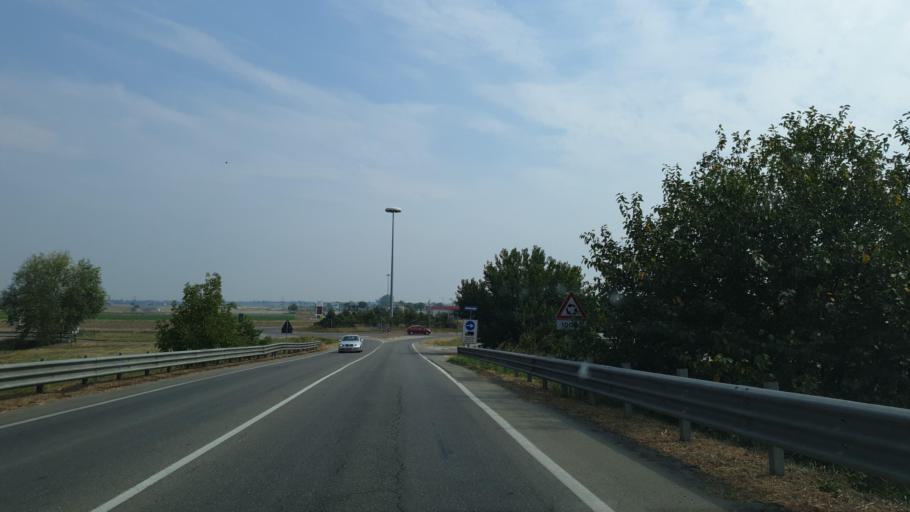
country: IT
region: Emilia-Romagna
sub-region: Provincia di Parma
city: Trecasali
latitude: 44.9164
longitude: 10.2569
